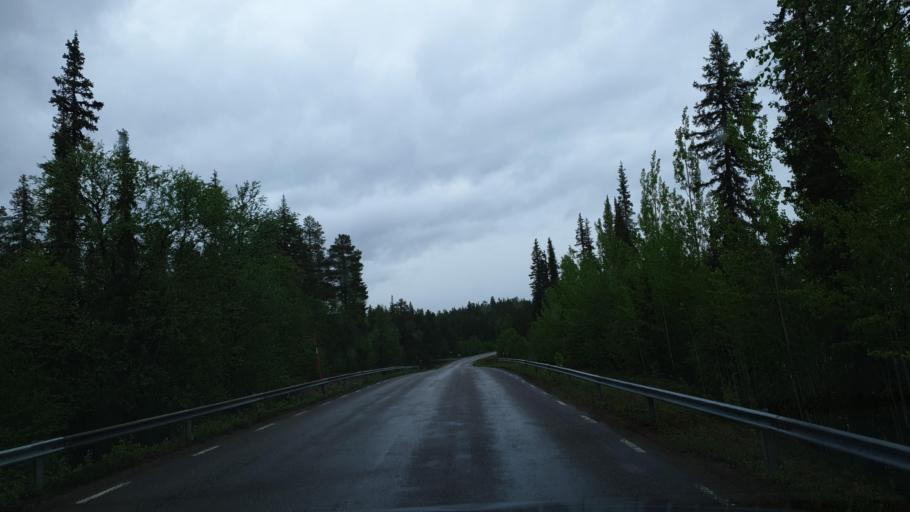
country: SE
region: Norrbotten
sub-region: Kiruna Kommun
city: Kiruna
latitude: 67.8869
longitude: 21.0140
